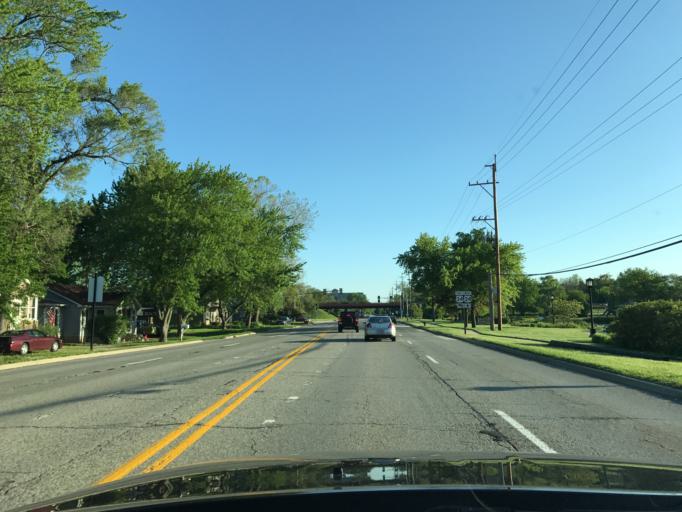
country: US
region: Illinois
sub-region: DuPage County
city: Lisle
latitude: 41.7987
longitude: -88.0773
